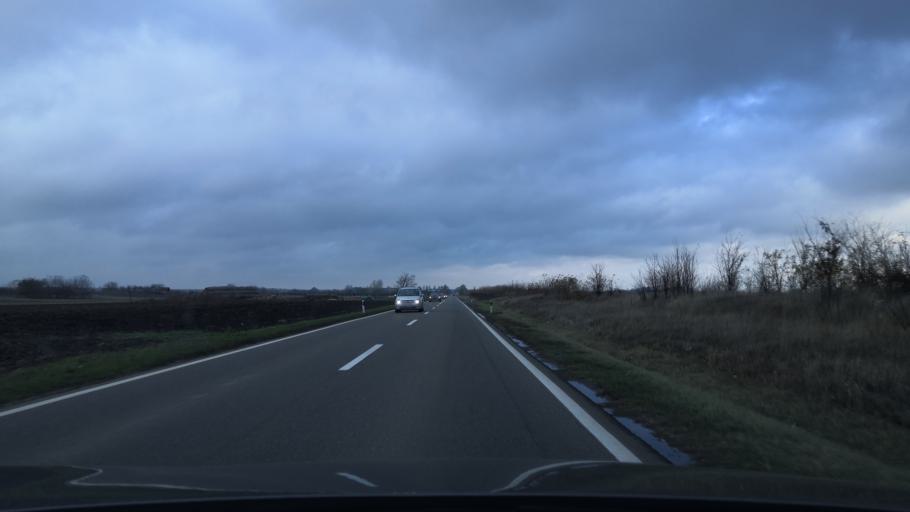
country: RS
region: Autonomna Pokrajina Vojvodina
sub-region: Severnobanatski Okrug
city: Novi Knezevac
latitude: 46.0132
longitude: 20.0981
